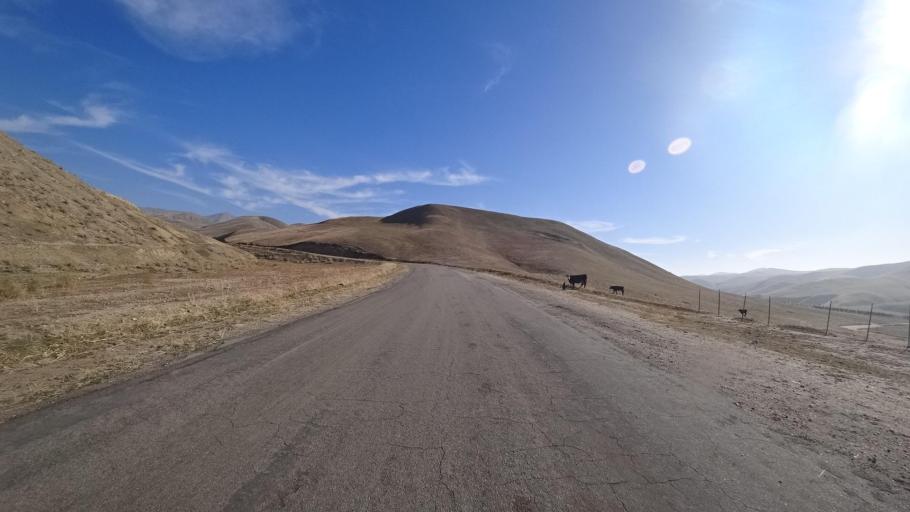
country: US
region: California
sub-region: Kern County
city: Lamont
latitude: 35.3940
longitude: -118.8070
